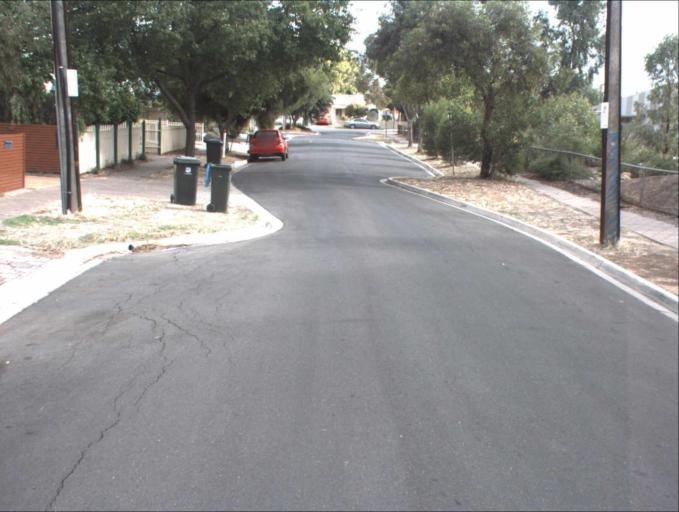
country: AU
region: South Australia
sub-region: Port Adelaide Enfield
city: Klemzig
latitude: -34.8663
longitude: 138.6378
